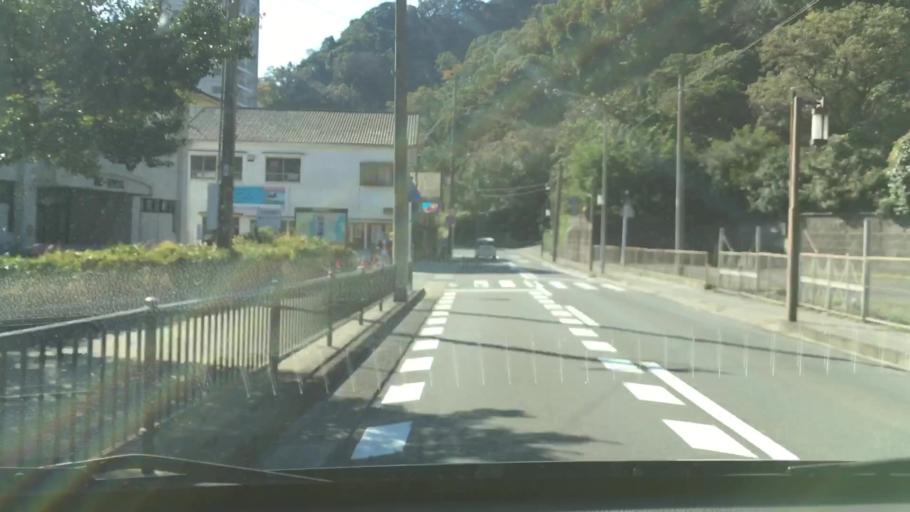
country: JP
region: Kagoshima
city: Kagoshima-shi
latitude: 31.6152
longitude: 130.5748
